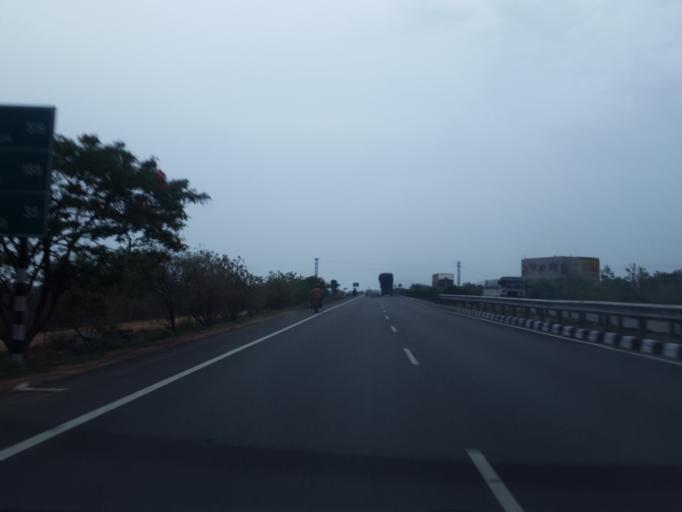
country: IN
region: Telangana
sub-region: Mahbubnagar
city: Farrukhnagar
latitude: 17.0783
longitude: 78.2287
